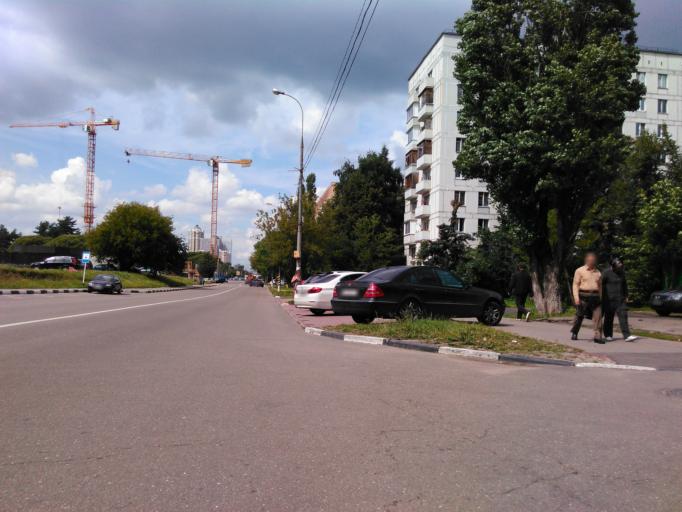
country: RU
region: Moskovskaya
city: Semenovskoye
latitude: 55.6720
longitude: 37.5280
